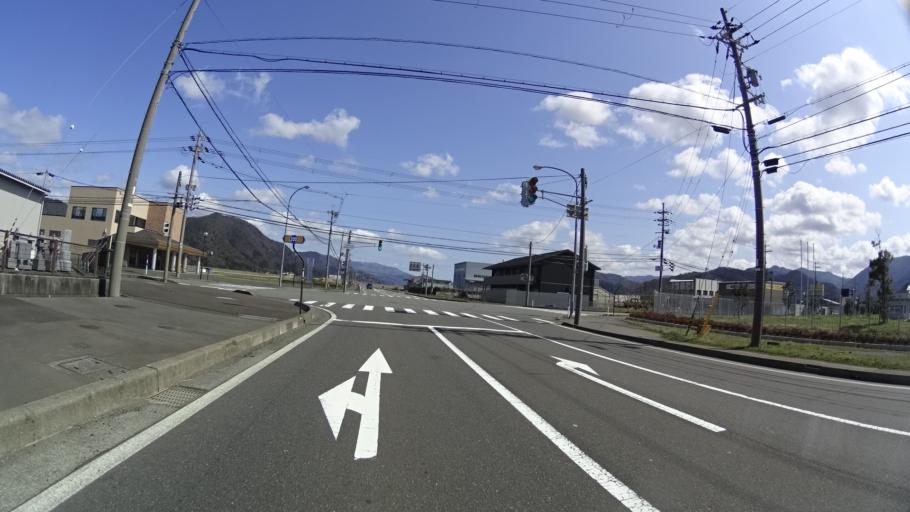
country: JP
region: Fukui
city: Obama
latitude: 35.4883
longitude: 135.7795
